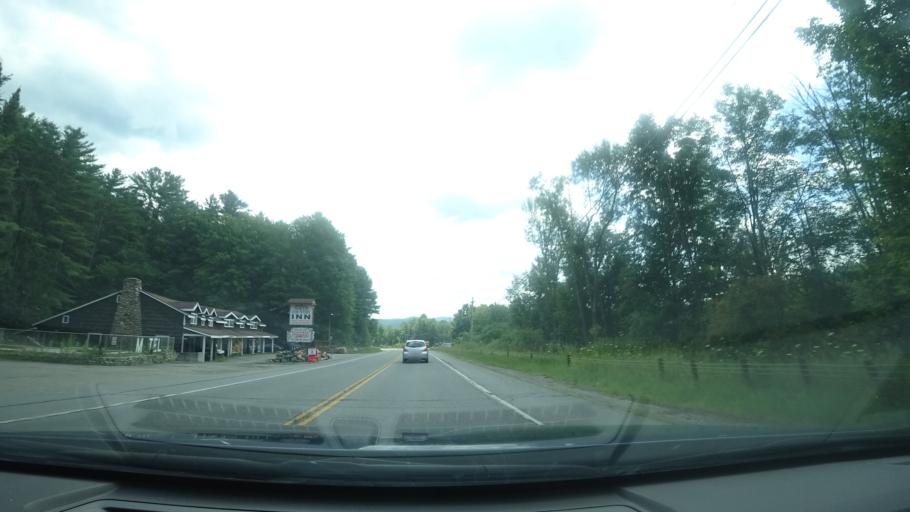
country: US
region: New York
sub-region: Warren County
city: Warrensburg
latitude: 43.5088
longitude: -73.7904
